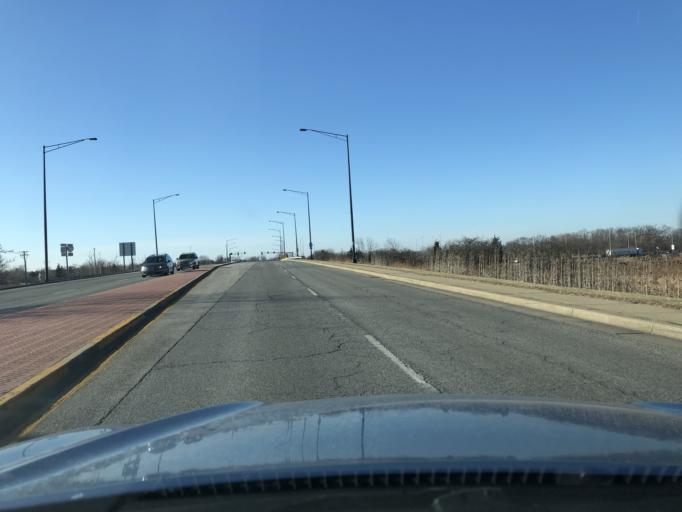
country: US
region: Illinois
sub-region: DuPage County
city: Itasca
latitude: 42.0035
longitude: -88.0240
